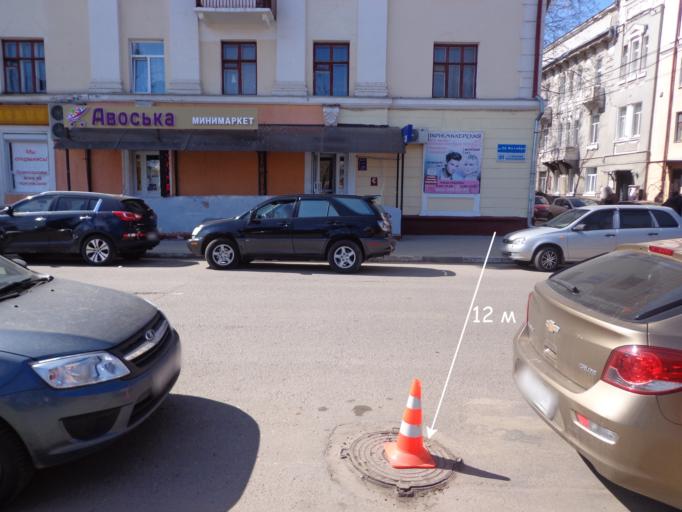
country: RU
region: Voronezj
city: Voronezh
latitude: 51.6650
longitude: 39.2106
